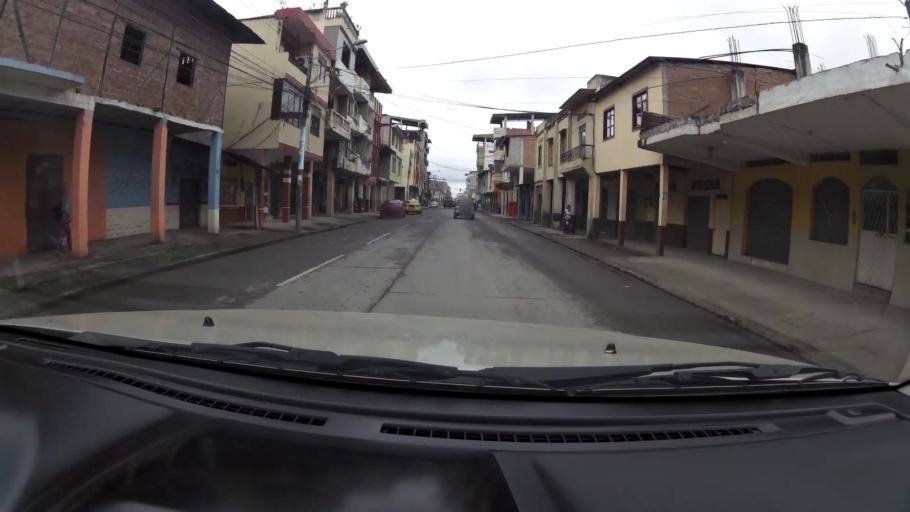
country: EC
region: El Oro
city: Pasaje
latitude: -3.3300
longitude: -79.8071
